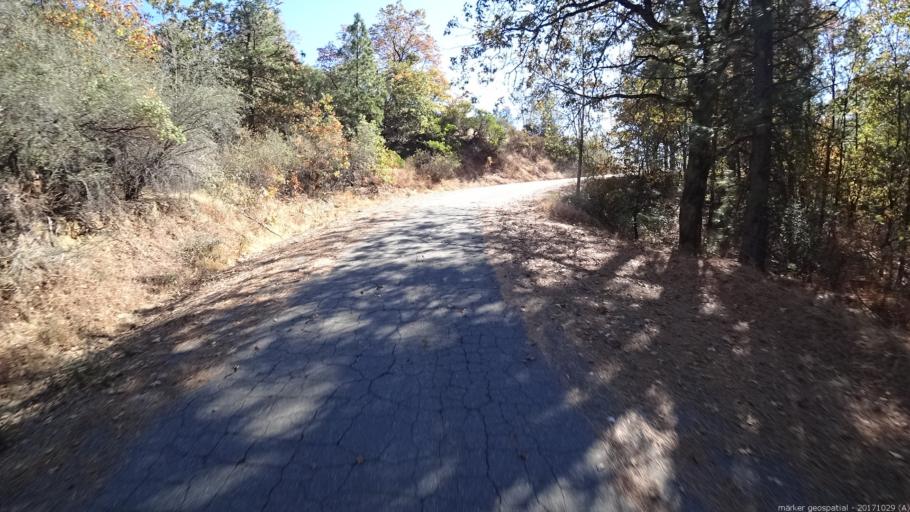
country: US
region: California
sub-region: Shasta County
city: Shasta
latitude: 40.4973
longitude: -122.6907
